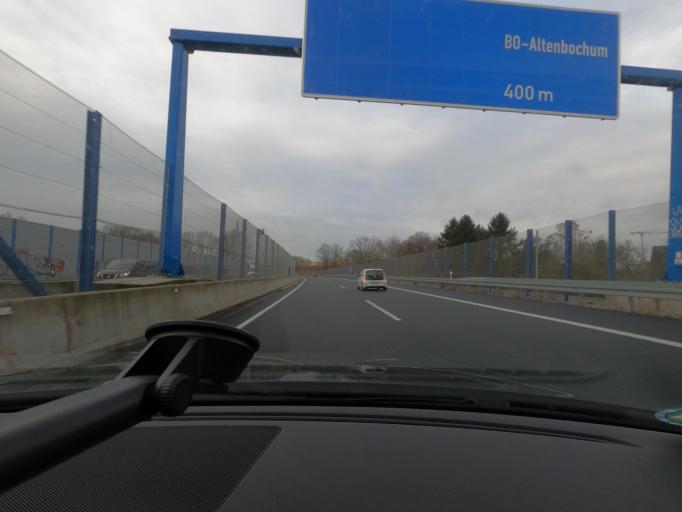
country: DE
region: North Rhine-Westphalia
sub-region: Regierungsbezirk Arnsberg
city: Bochum
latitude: 51.4644
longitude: 7.2737
